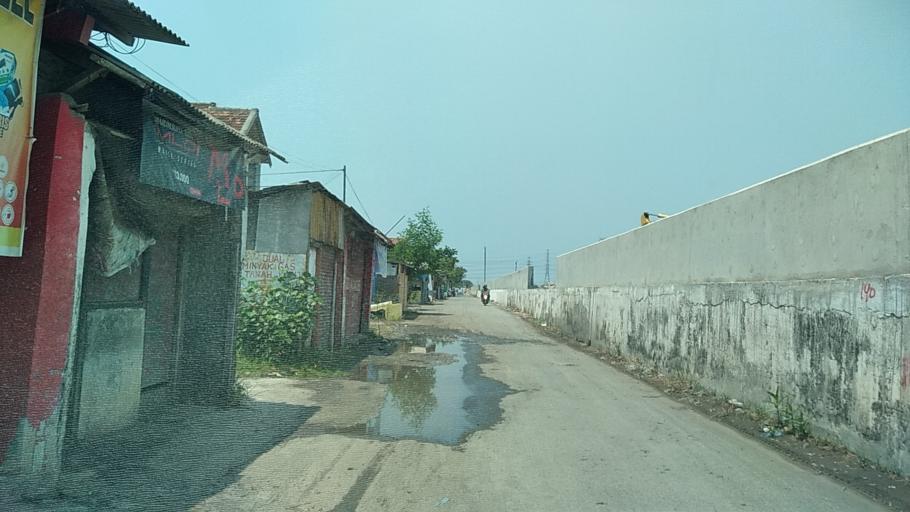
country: ID
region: Central Java
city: Semarang
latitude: -6.9582
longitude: 110.4415
